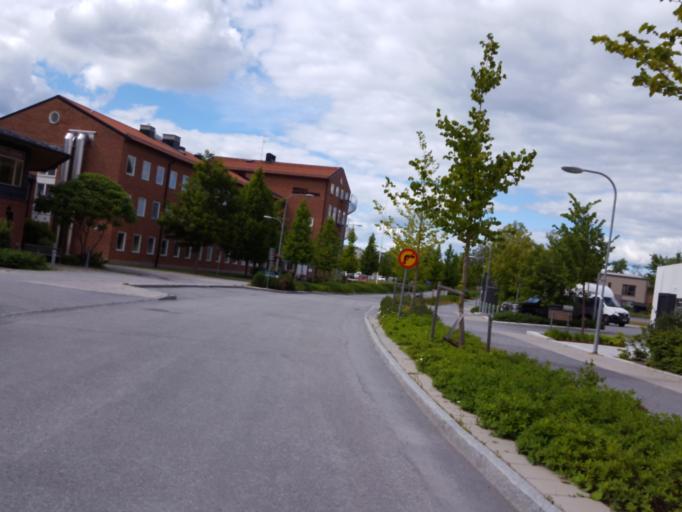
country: SE
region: Uppsala
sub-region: Uppsala Kommun
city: Uppsala
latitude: 59.8480
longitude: 17.6350
